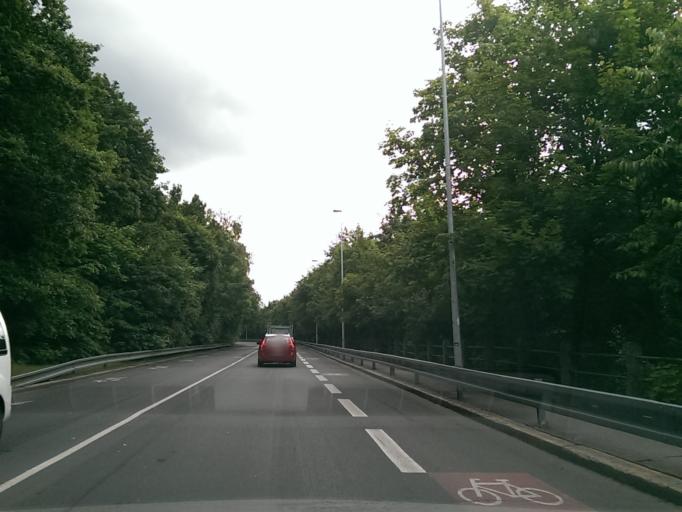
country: CZ
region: Praha
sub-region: Praha 4
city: Hodkovicky
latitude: 50.0303
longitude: 14.4288
